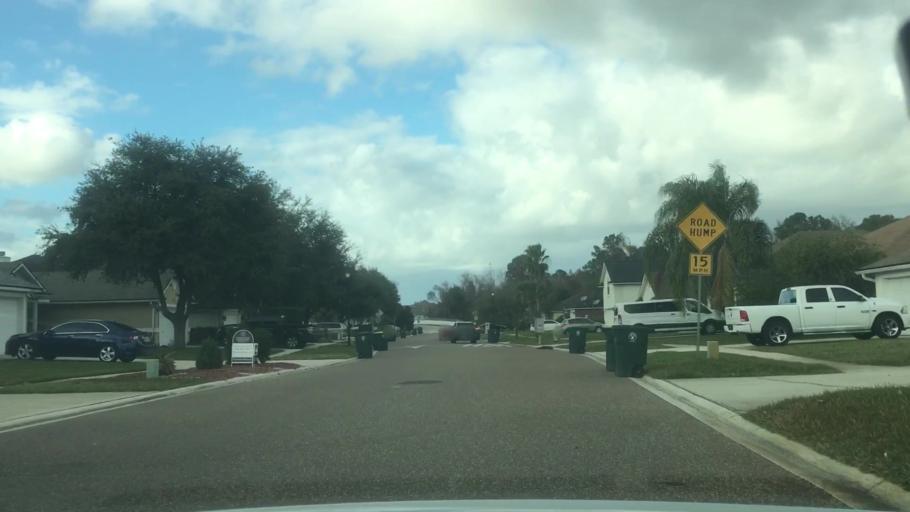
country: US
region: Florida
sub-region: Duval County
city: Neptune Beach
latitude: 30.3046
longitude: -81.5036
